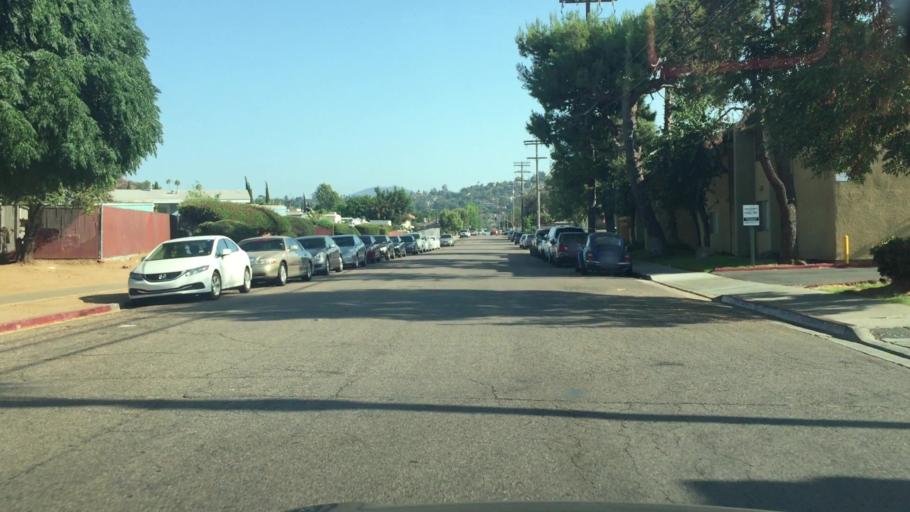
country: US
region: California
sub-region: San Diego County
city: El Cajon
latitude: 32.7907
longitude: -116.9482
